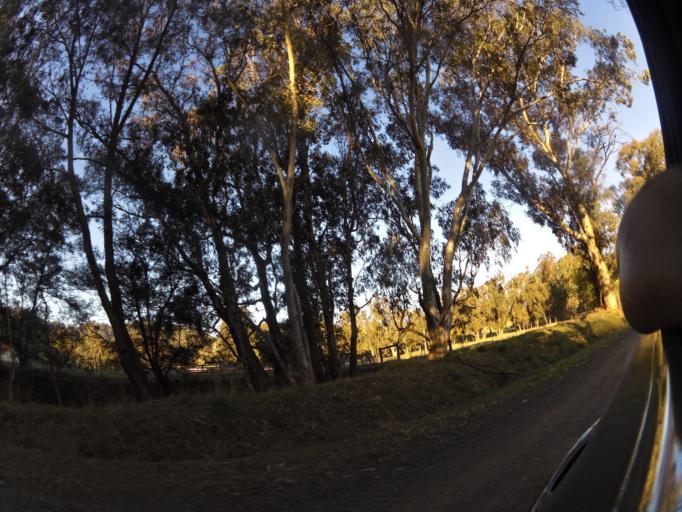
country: AU
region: Victoria
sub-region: Murrindindi
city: Alexandra
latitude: -37.1479
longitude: 145.5280
